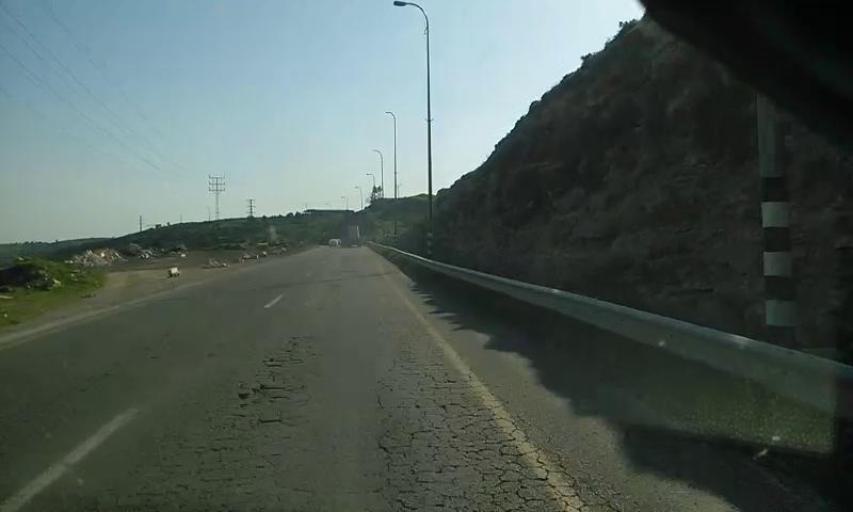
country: PS
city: Khallat ad Dar
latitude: 31.5109
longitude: 35.1320
